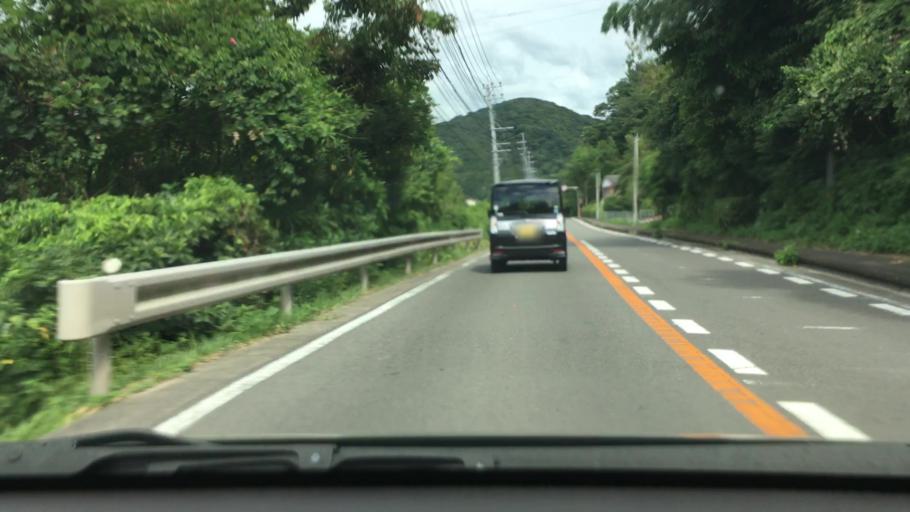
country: JP
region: Nagasaki
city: Togitsu
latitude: 32.8614
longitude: 129.7996
